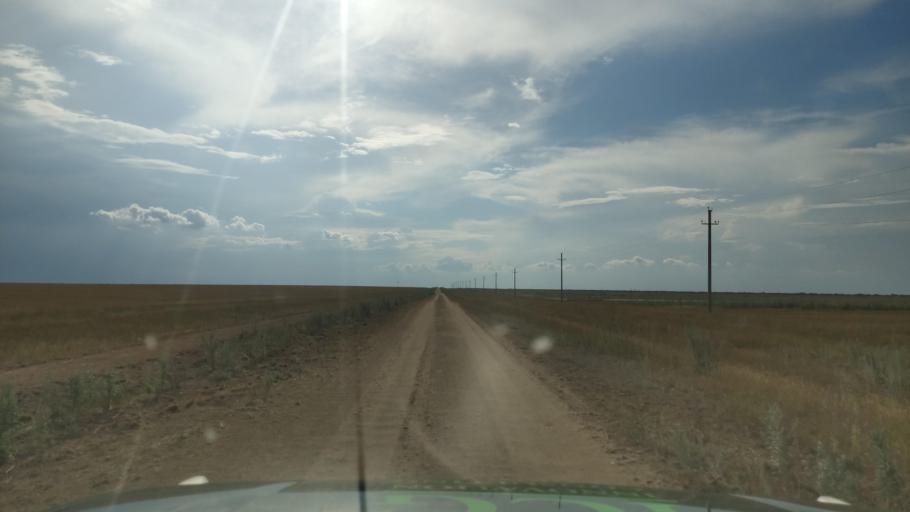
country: KZ
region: Pavlodar
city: Pavlodar
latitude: 52.5091
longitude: 77.5714
